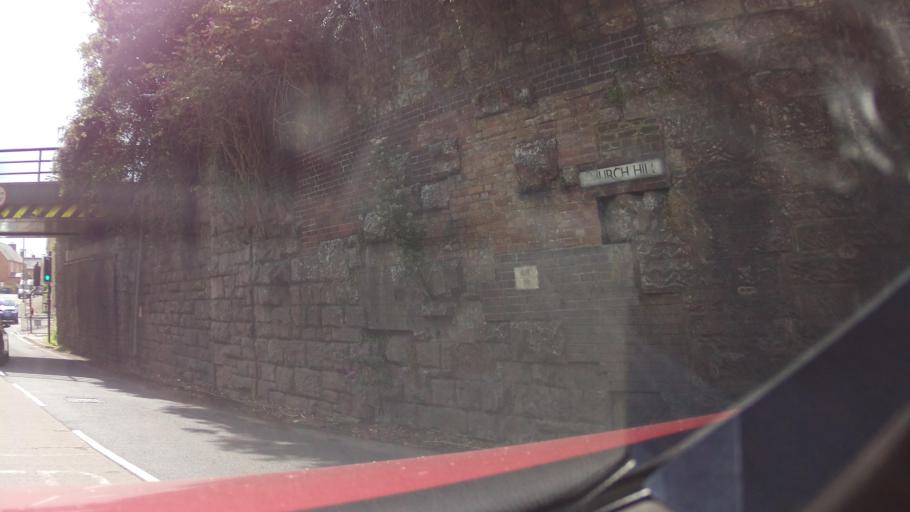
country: GB
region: England
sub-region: Somerset
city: Wincanton
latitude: 51.0022
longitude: -2.4164
